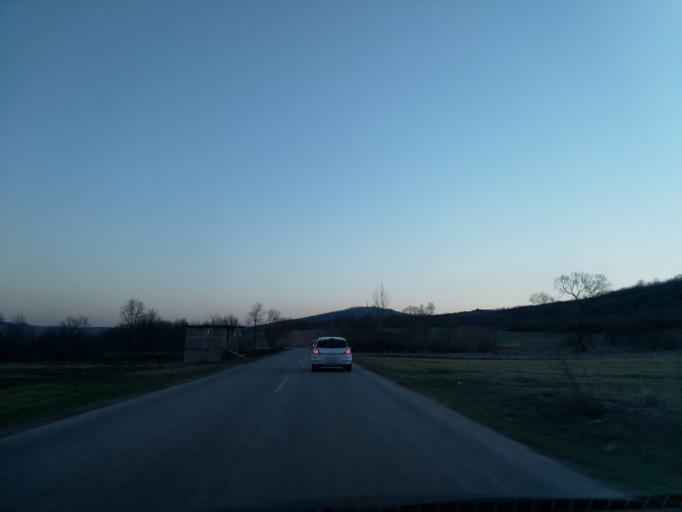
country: RS
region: Central Serbia
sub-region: Pomoravski Okrug
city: Paracin
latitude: 43.8768
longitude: 21.4708
